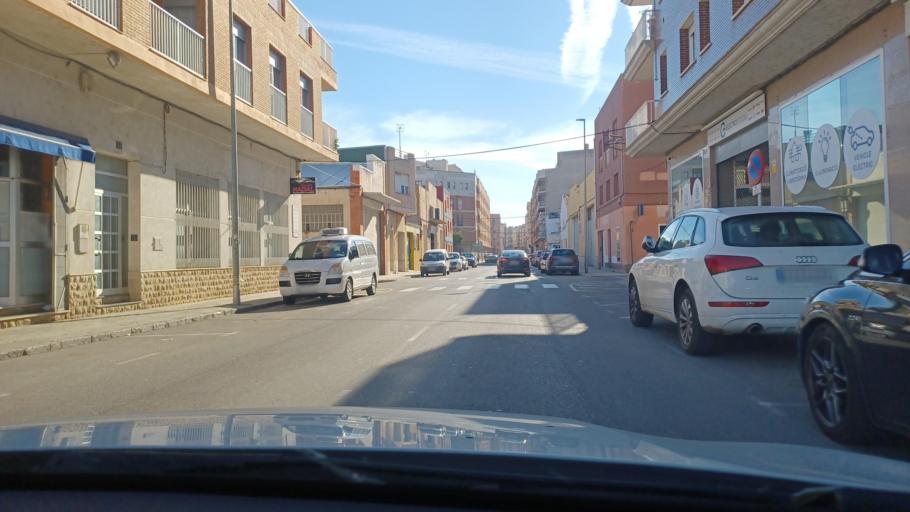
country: ES
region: Catalonia
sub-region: Provincia de Tarragona
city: Amposta
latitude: 40.7070
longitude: 0.5806
